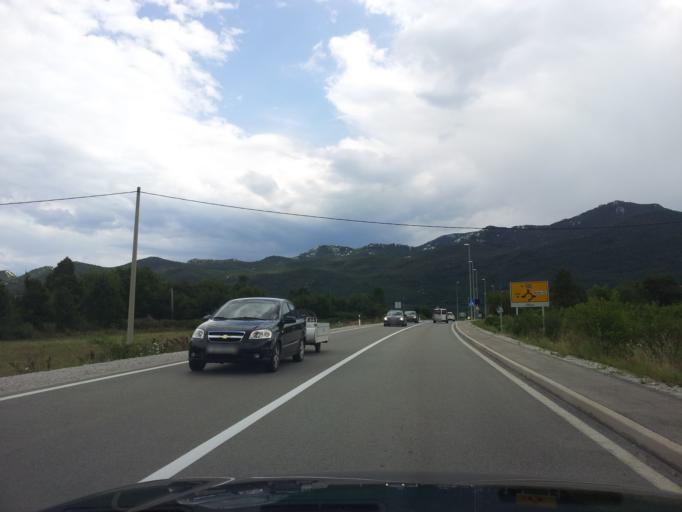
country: HR
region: Zadarska
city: Gracac
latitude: 44.3022
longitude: 15.8612
